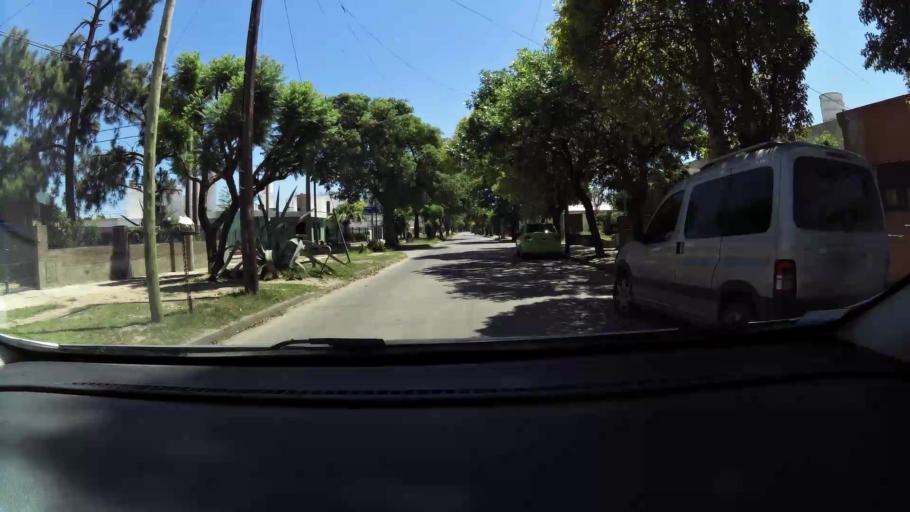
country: AR
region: Cordoba
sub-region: Departamento de Capital
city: Cordoba
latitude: -31.4302
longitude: -64.1273
